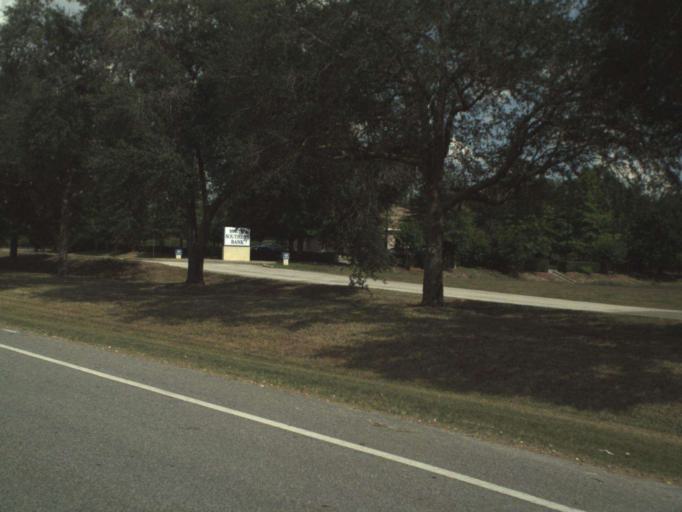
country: US
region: Florida
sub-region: Lake County
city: Mount Dora
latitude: 28.8239
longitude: -81.6418
